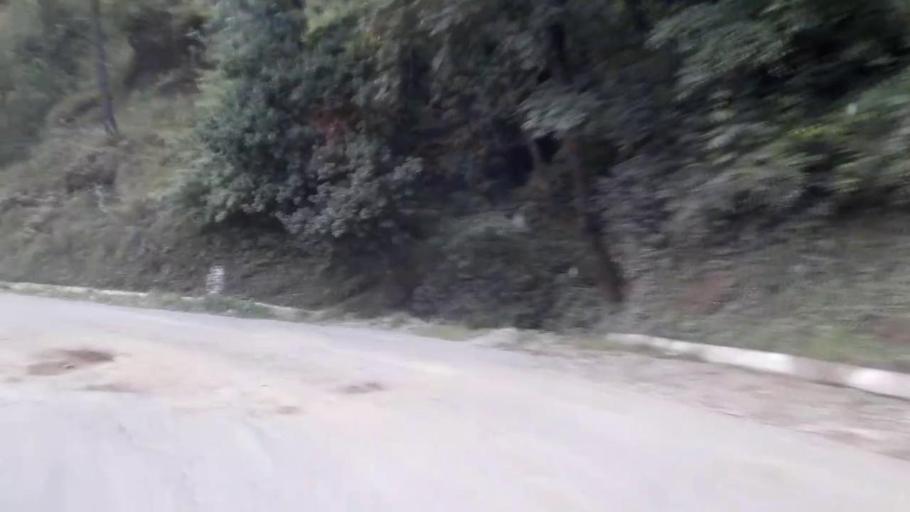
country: IN
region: Himachal Pradesh
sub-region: Shimla
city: Jutogh
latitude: 31.0500
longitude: 77.1442
